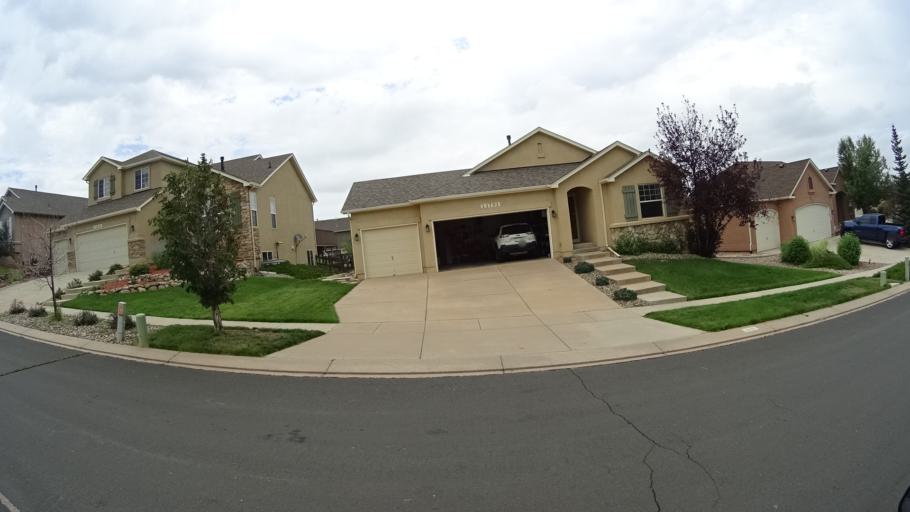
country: US
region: Colorado
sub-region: El Paso County
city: Gleneagle
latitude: 39.0028
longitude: -104.7922
